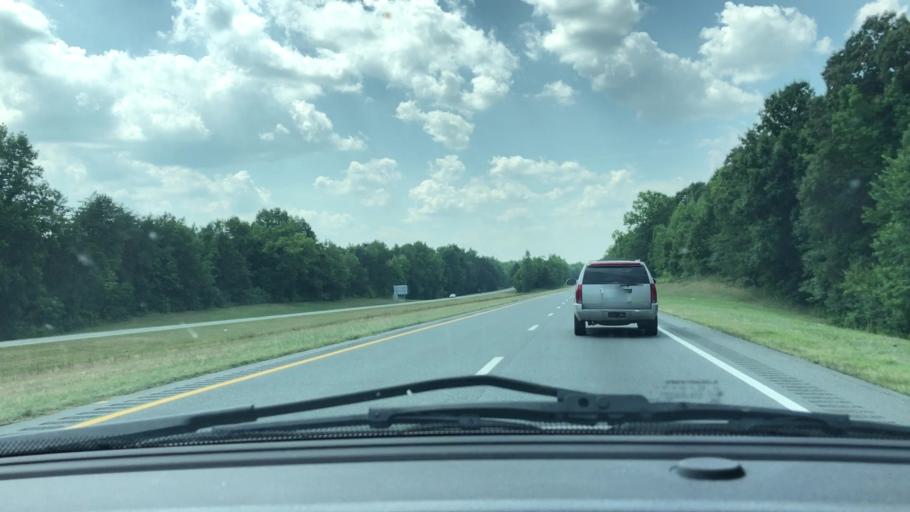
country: US
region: North Carolina
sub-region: Guilford County
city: Forest Oaks
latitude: 35.9727
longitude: -79.7216
